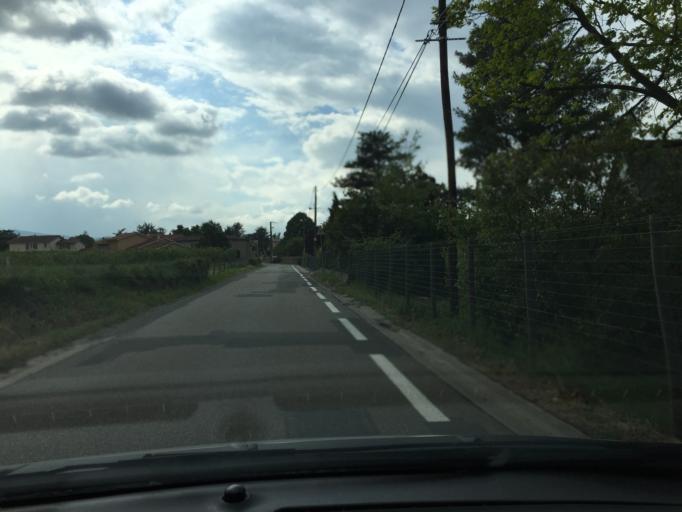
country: FR
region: Rhone-Alpes
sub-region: Departement du Rhone
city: Orlienas
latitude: 45.6645
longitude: 4.7221
